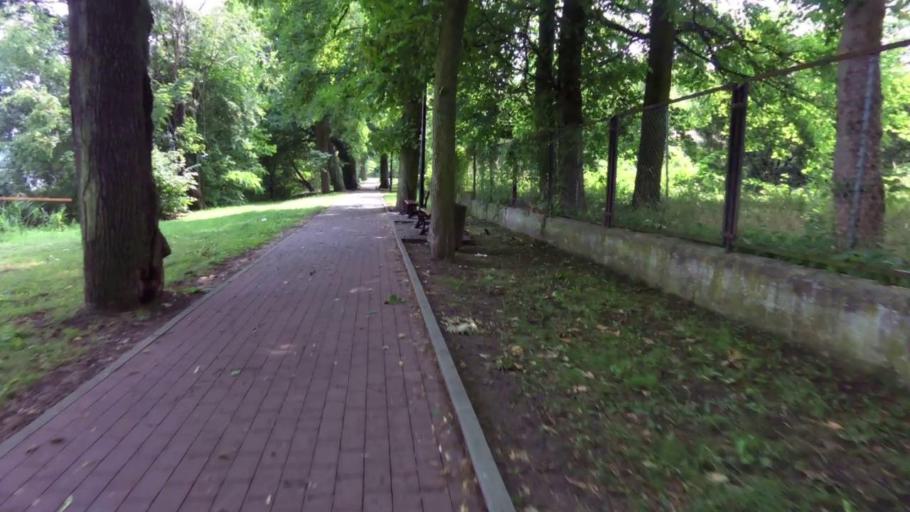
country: PL
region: West Pomeranian Voivodeship
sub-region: Powiat choszczenski
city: Choszczno
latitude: 53.1635
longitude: 15.4089
